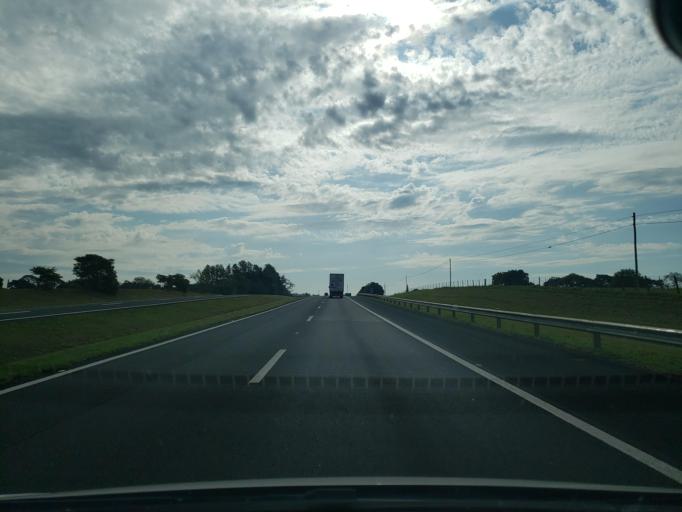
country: BR
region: Sao Paulo
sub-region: Birigui
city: Birigui
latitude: -21.3335
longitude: -50.3318
